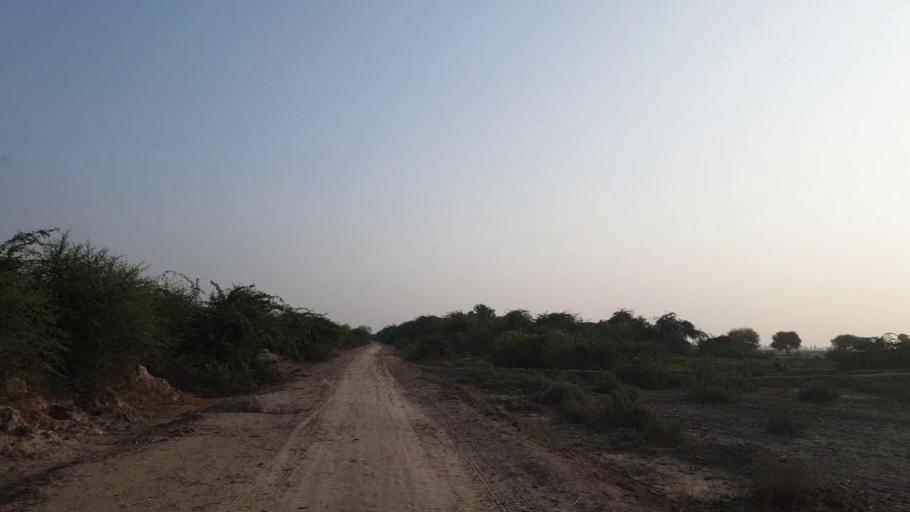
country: PK
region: Sindh
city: Kario
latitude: 24.8752
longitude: 68.6205
